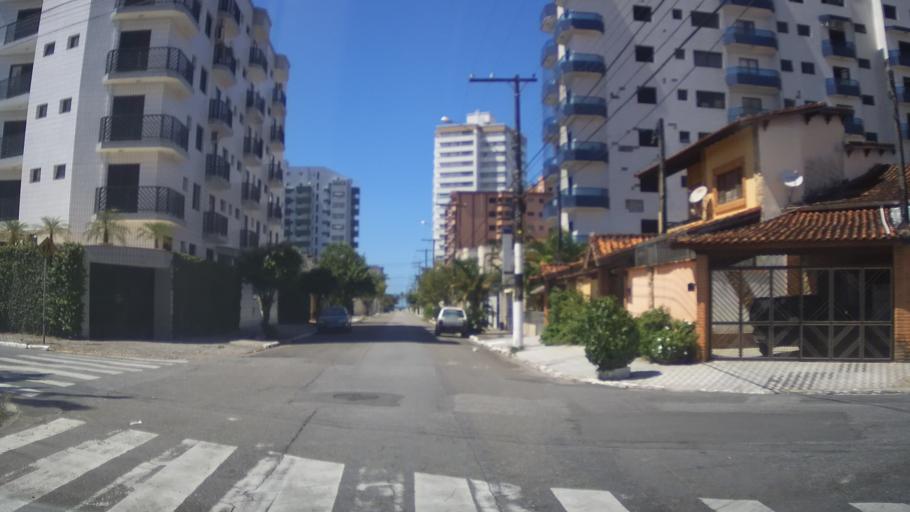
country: BR
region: Sao Paulo
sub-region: Mongagua
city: Mongagua
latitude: -24.0469
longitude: -46.5266
